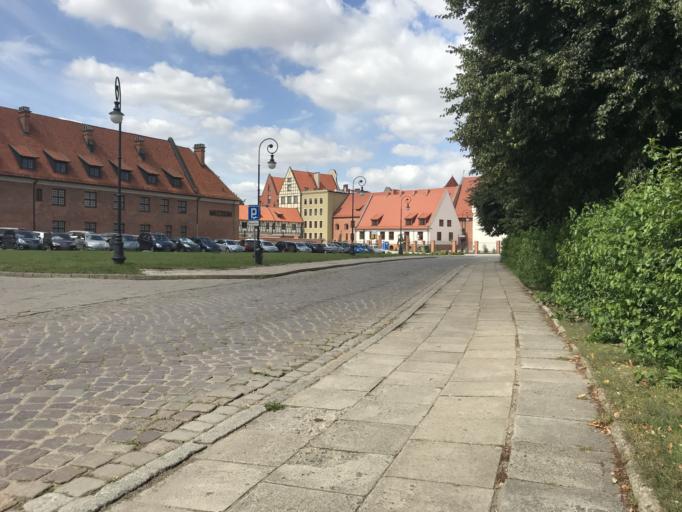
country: PL
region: Warmian-Masurian Voivodeship
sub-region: Powiat elblaski
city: Elblag
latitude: 54.1565
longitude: 19.3960
